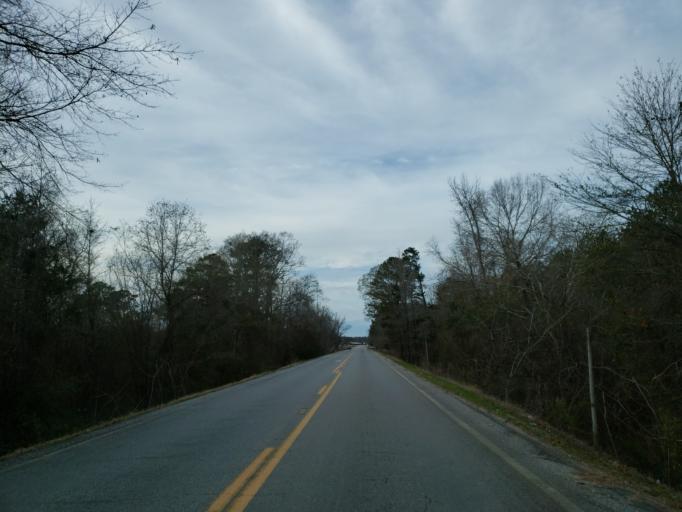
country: US
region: Mississippi
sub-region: Clarke County
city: Quitman
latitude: 31.8736
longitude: -88.7057
